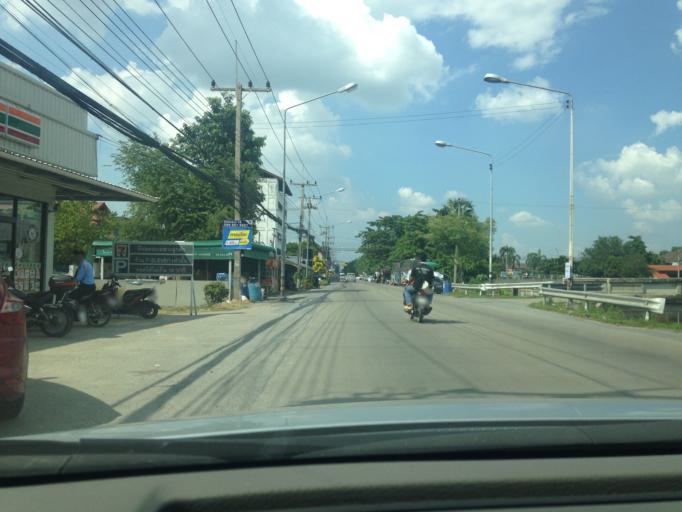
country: TH
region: Phra Nakhon Si Ayutthaya
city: Ban Bang Kadi Pathum Thani
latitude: 13.9898
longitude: 100.5990
